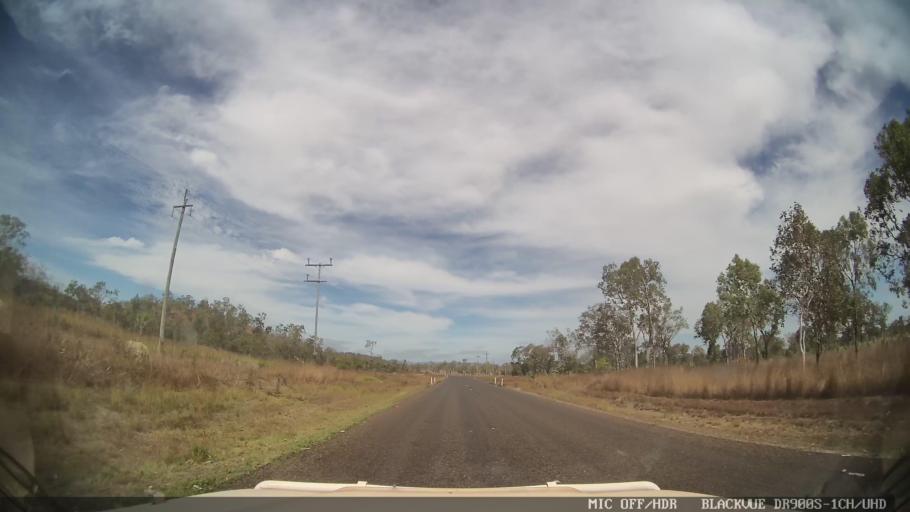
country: AU
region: Queensland
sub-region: Tablelands
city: Mareeba
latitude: -16.8485
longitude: 145.3818
